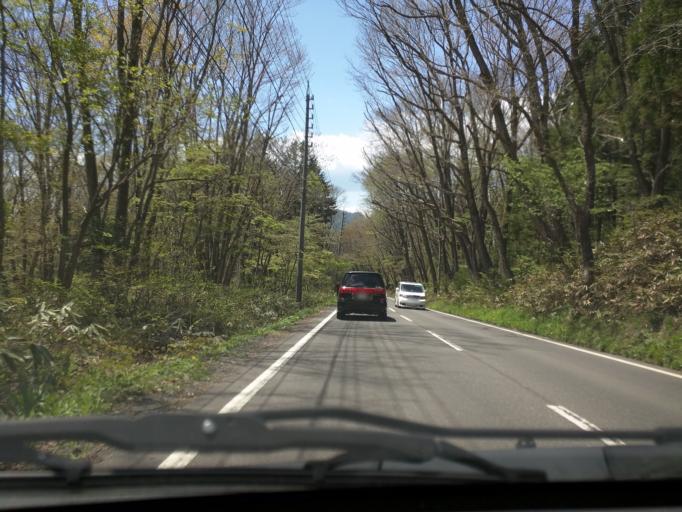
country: JP
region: Nagano
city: Nagano-shi
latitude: 36.7350
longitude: 138.0830
